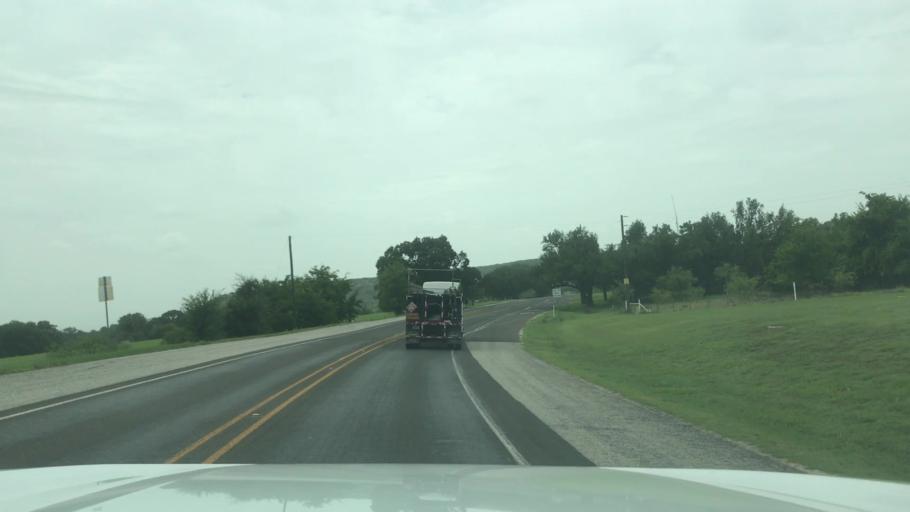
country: US
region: Texas
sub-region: Bosque County
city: Meridian
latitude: 31.9124
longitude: -97.6617
